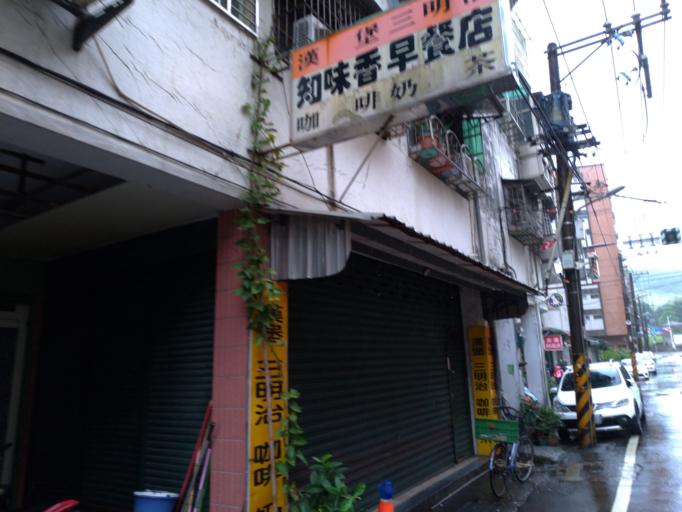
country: TW
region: Taiwan
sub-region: Keelung
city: Keelung
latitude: 25.0863
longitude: 121.6956
